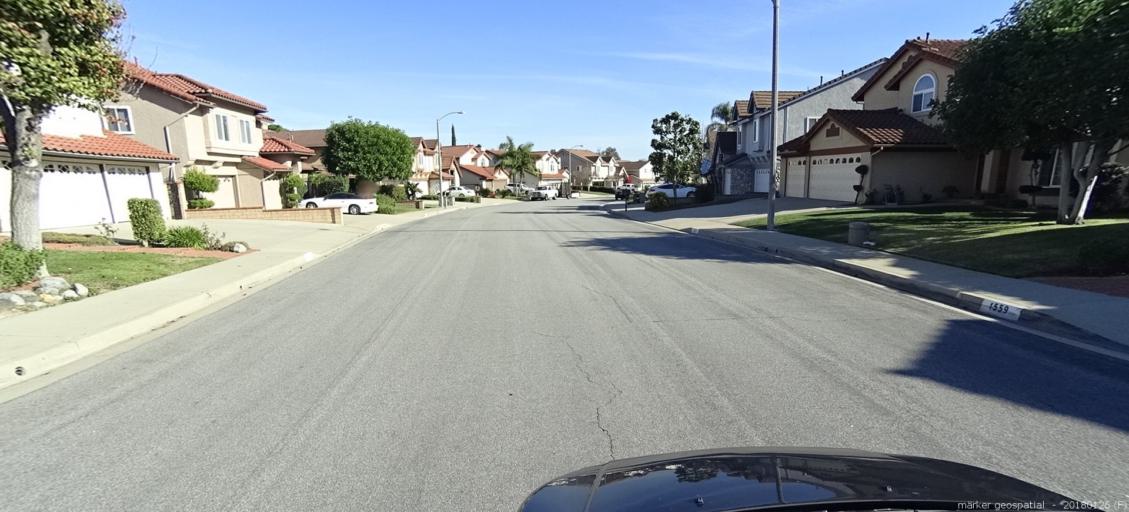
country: US
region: California
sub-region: Los Angeles County
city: Diamond Bar
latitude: 33.9943
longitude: -117.7969
